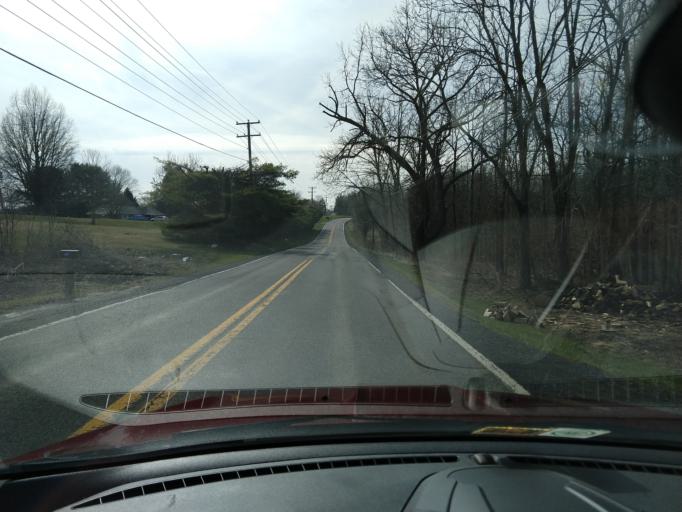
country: US
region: West Virginia
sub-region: Greenbrier County
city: Lewisburg
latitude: 37.8723
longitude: -80.4116
